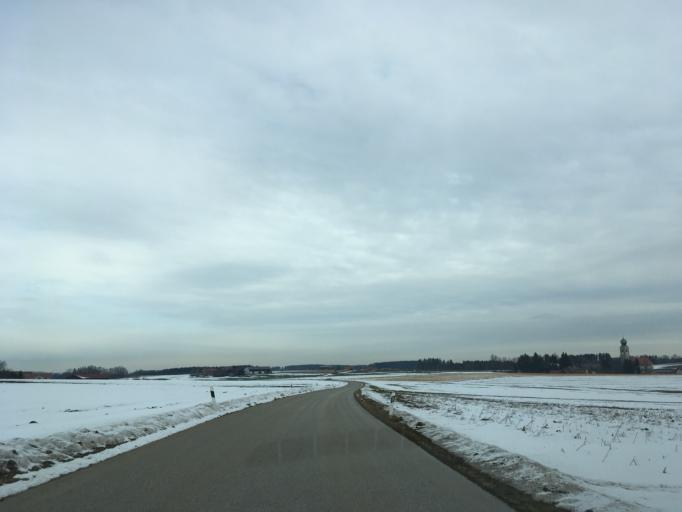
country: DE
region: Bavaria
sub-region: Upper Bavaria
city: Jettenbach
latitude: 48.1362
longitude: 12.3883
